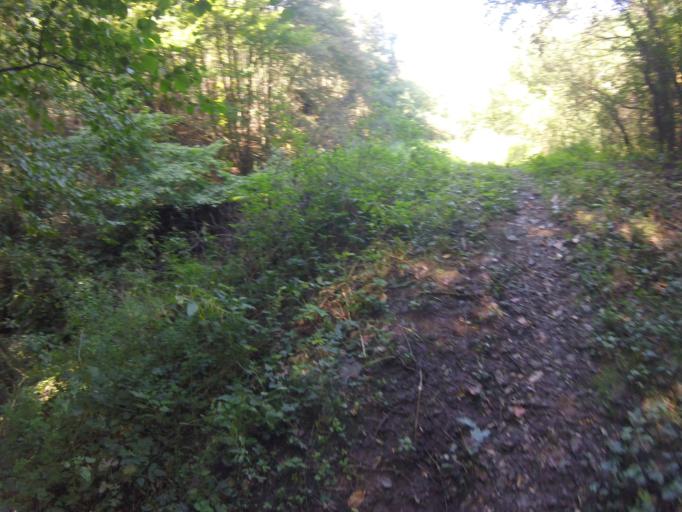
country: HU
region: Nograd
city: Bujak
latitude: 47.8979
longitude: 19.5215
